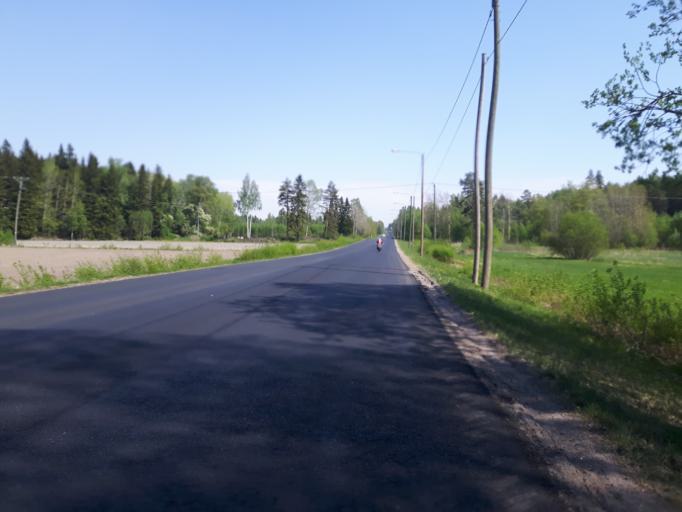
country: FI
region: Uusimaa
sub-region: Helsinki
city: Nickby
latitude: 60.3179
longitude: 25.4066
